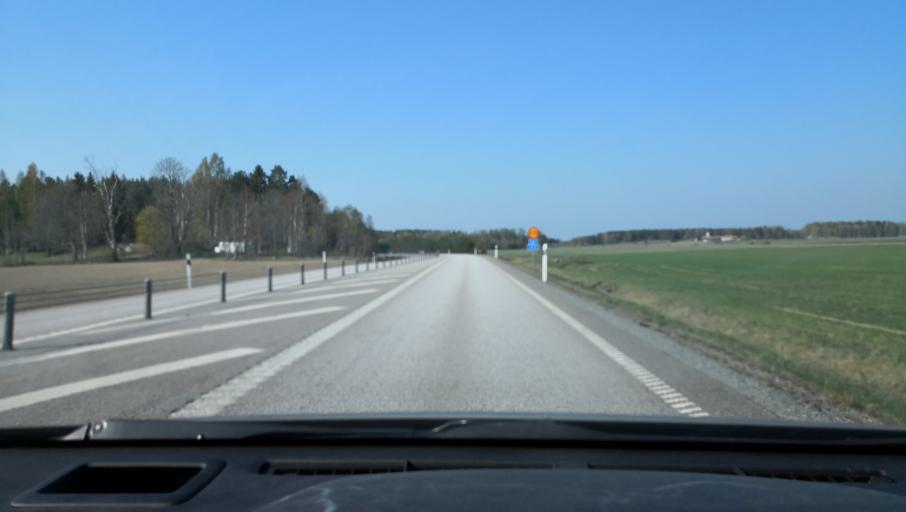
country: SE
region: Uppsala
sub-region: Heby Kommun
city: Tarnsjo
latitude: 60.2514
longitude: 16.9598
